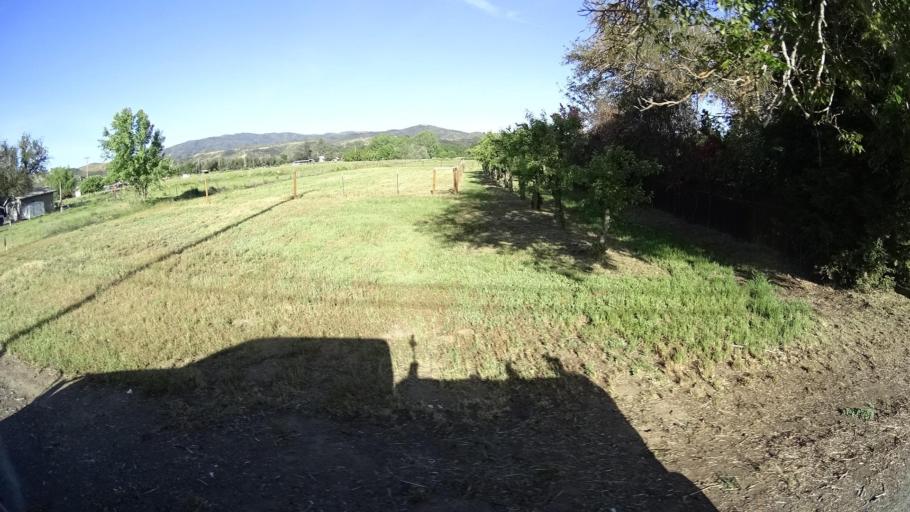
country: US
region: California
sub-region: Lake County
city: North Lakeport
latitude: 39.0754
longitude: -122.9498
